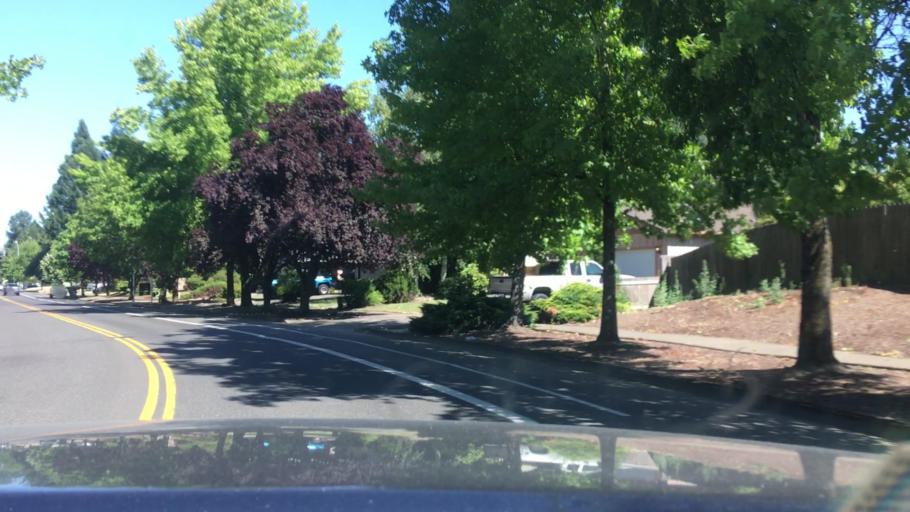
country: US
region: Oregon
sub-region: Lane County
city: Eugene
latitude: 44.0929
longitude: -123.0842
